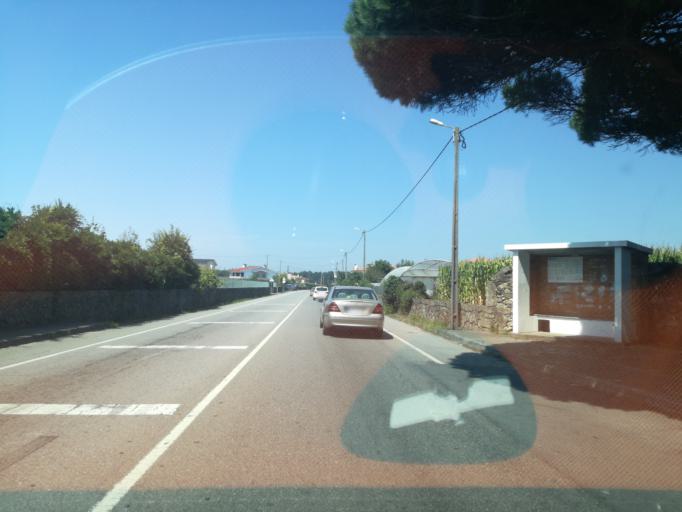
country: PT
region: Braga
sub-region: Esposende
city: Apulia
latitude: 41.4739
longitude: -8.7466
